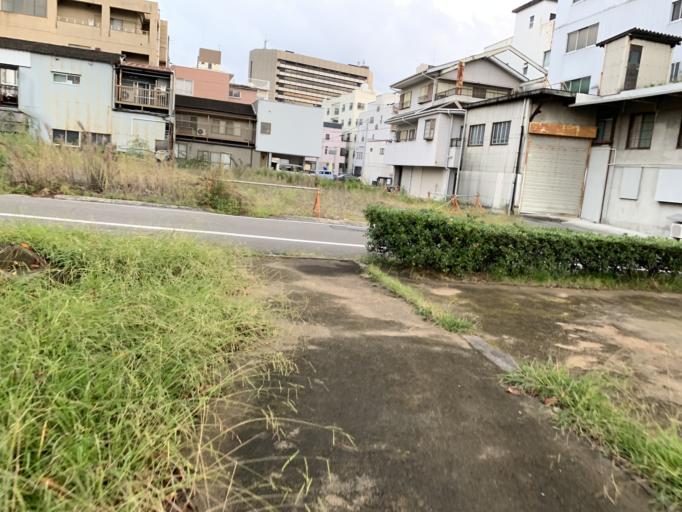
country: JP
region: Tokushima
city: Tokushima-shi
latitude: 34.0677
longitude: 134.5541
